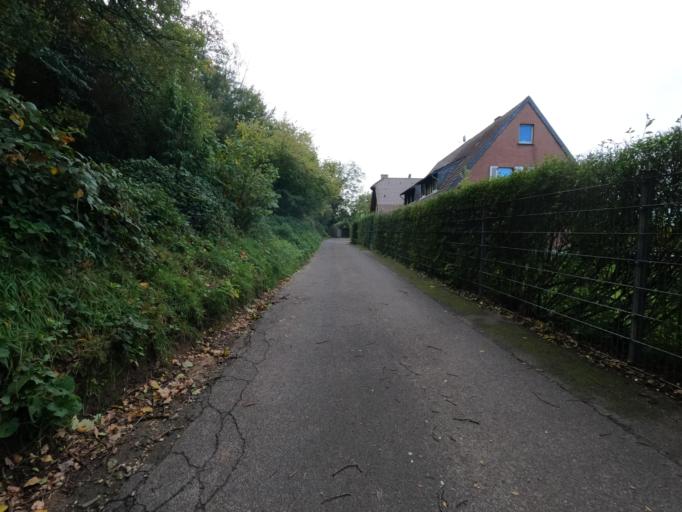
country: DE
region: North Rhine-Westphalia
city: Huckelhoven
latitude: 51.0479
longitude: 6.2513
